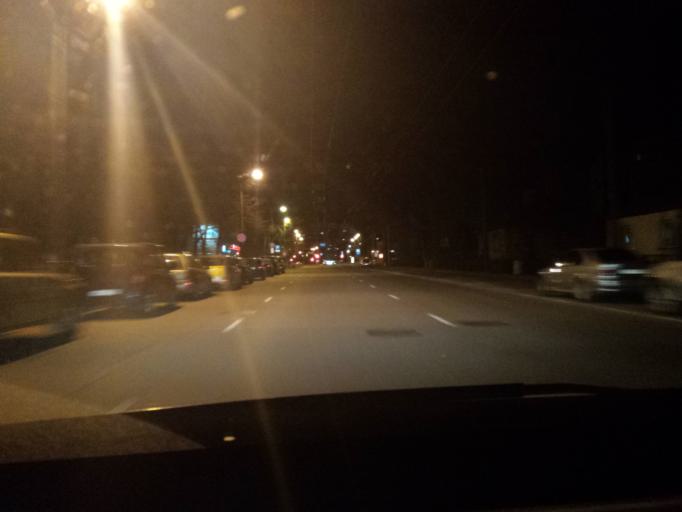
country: LV
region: Riga
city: Riga
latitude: 56.9621
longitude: 24.1720
